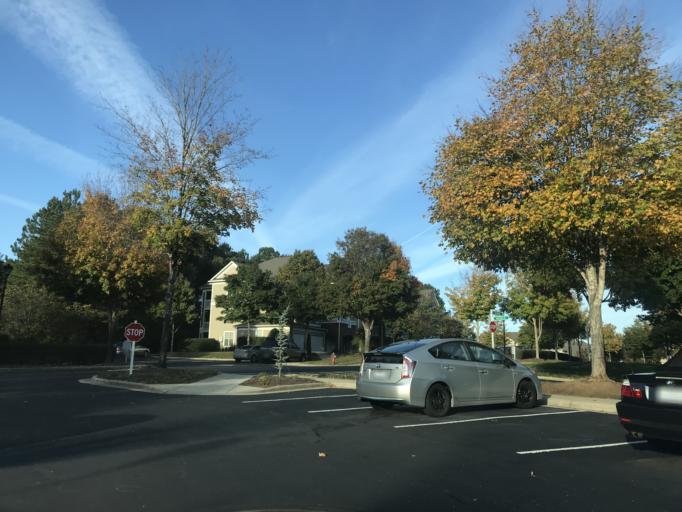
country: US
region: North Carolina
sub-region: Wake County
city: Wake Forest
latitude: 35.9084
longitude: -78.5964
